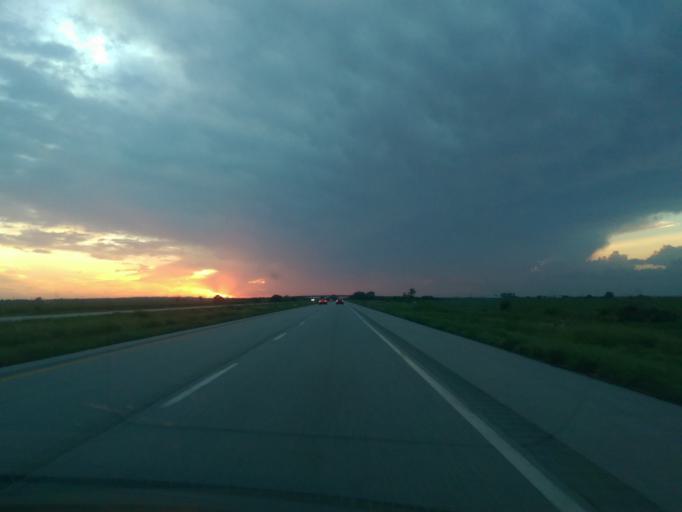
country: US
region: Iowa
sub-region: Fremont County
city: Hamburg
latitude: 40.6349
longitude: -95.7266
